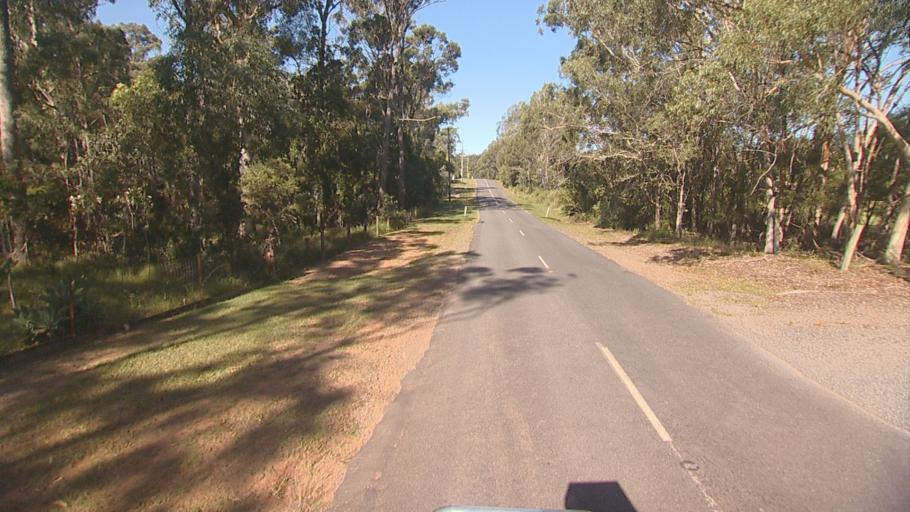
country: AU
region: Queensland
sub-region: Logan
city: Springwood
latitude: -27.5957
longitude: 153.1597
